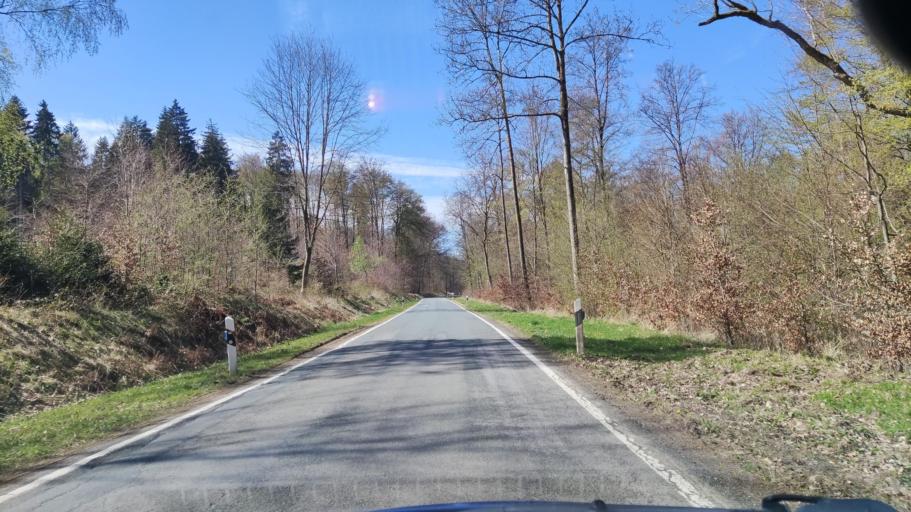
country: DE
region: Lower Saxony
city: Eimen
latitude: 51.9003
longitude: 9.7980
